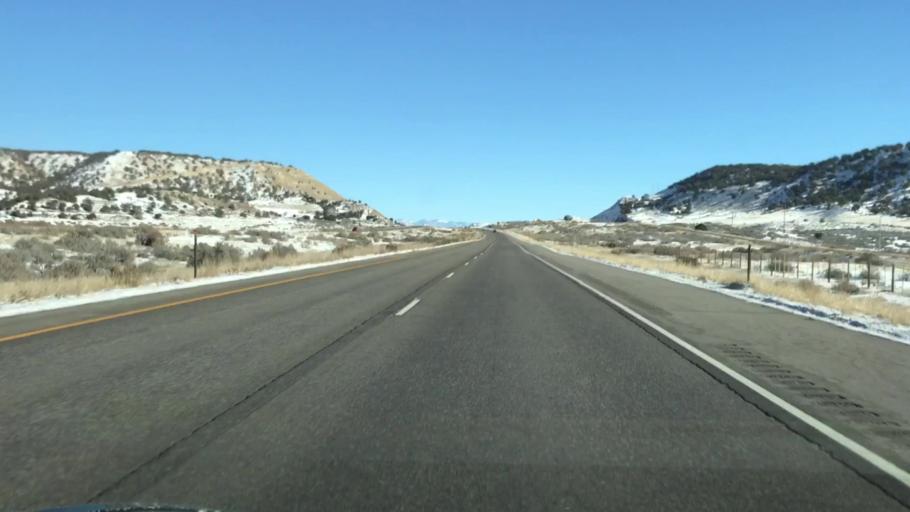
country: US
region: Colorado
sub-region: Garfield County
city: Rifle
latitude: 39.5051
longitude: -107.8910
